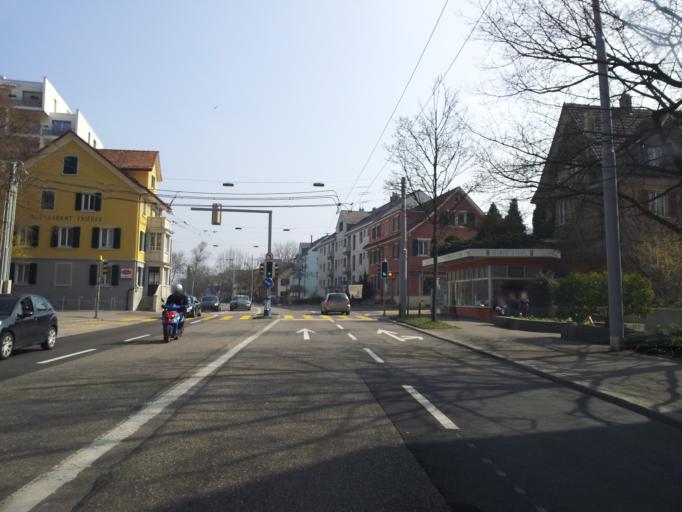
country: CH
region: Zurich
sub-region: Bezirk Zuerich
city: Zuerich (Kreis 11) / Affoltern
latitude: 47.4159
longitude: 8.5123
